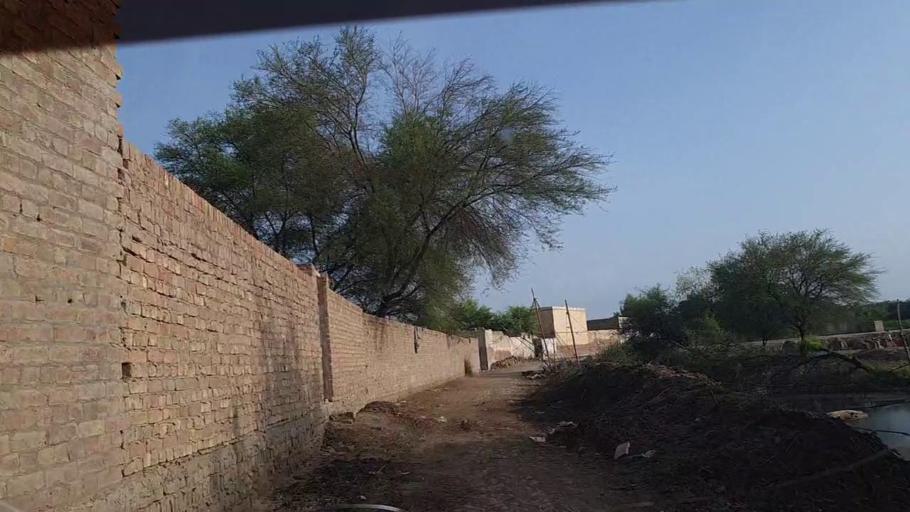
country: PK
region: Sindh
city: Ghotki
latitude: 27.9773
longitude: 69.2576
